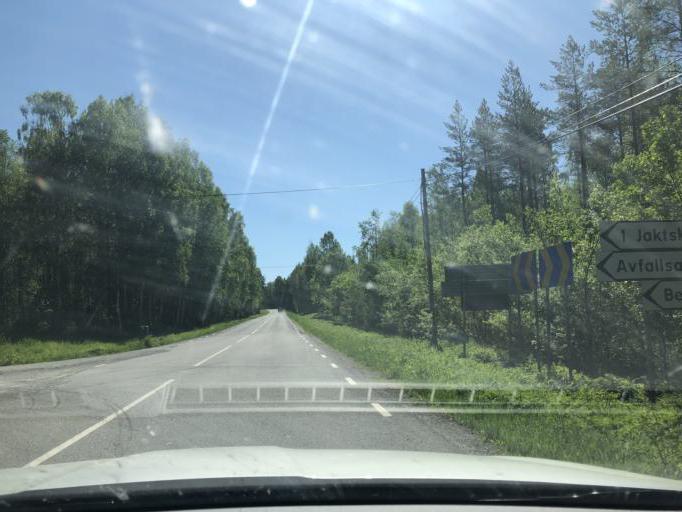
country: SE
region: Norrbotten
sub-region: Lulea Kommun
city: Sodra Sunderbyn
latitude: 65.6636
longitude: 21.9702
